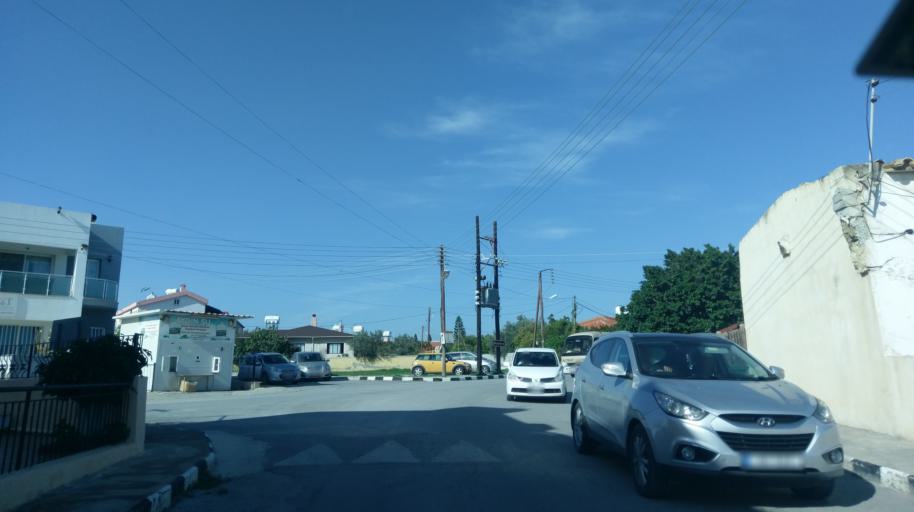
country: CY
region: Ammochostos
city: Trikomo
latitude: 35.2884
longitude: 33.8914
